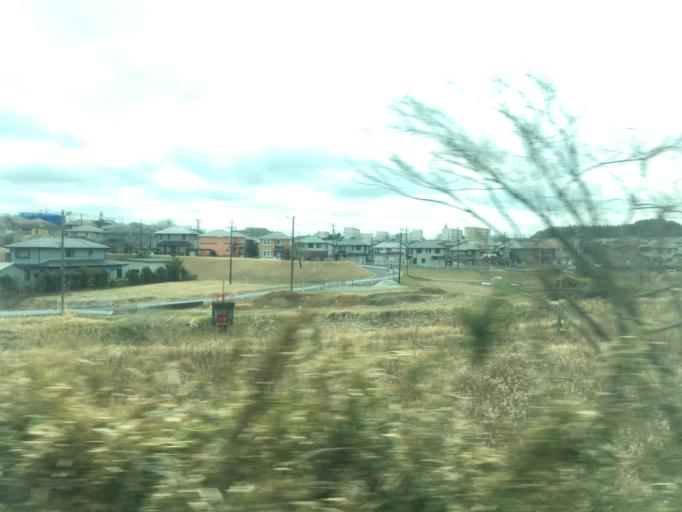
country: JP
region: Chiba
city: Narita
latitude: 35.7873
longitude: 140.3031
